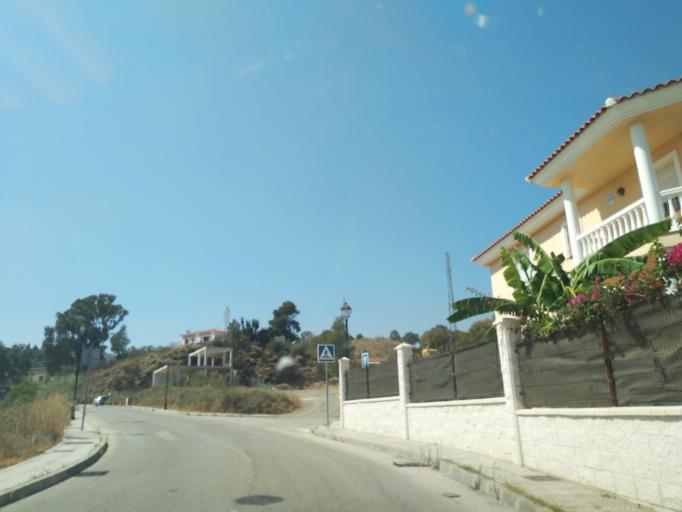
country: ES
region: Andalusia
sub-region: Provincia de Malaga
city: Valdes
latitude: 36.7210
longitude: -4.1975
